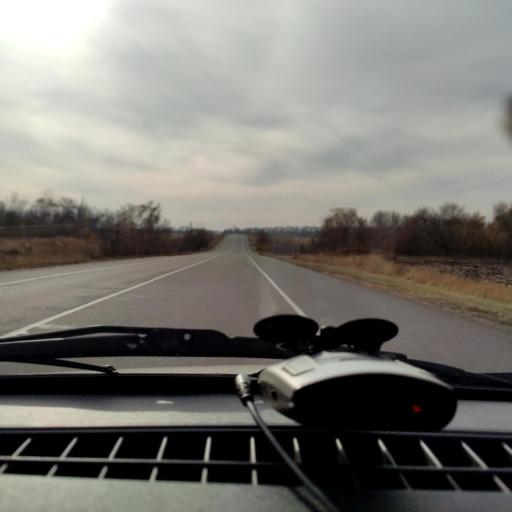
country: RU
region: Voronezj
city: Devitsa
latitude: 51.5805
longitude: 38.9757
